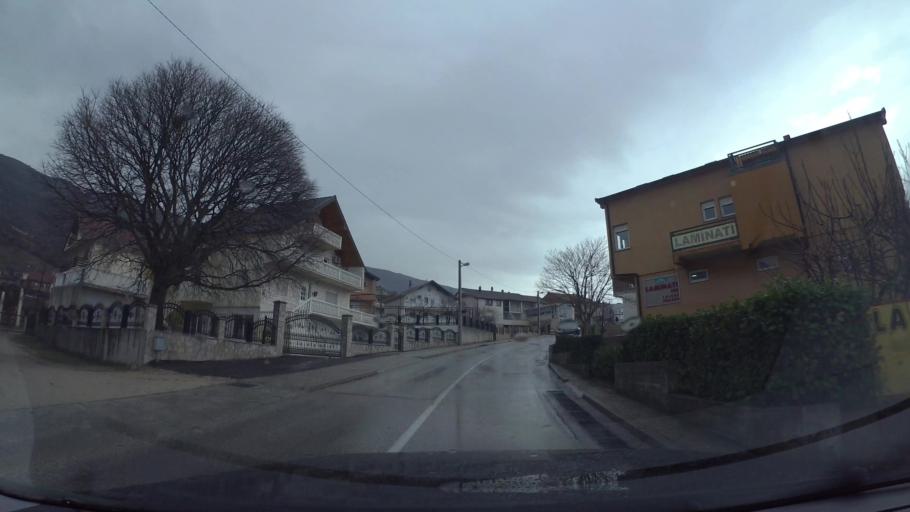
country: BA
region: Federation of Bosnia and Herzegovina
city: Rodoc
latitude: 43.3183
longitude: 17.8347
